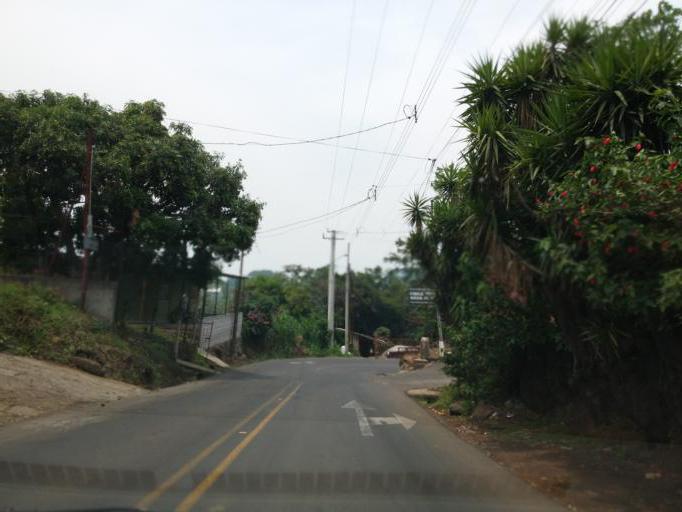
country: CR
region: Heredia
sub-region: Canton de Belen
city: San Antonio
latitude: 9.9927
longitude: -84.1994
